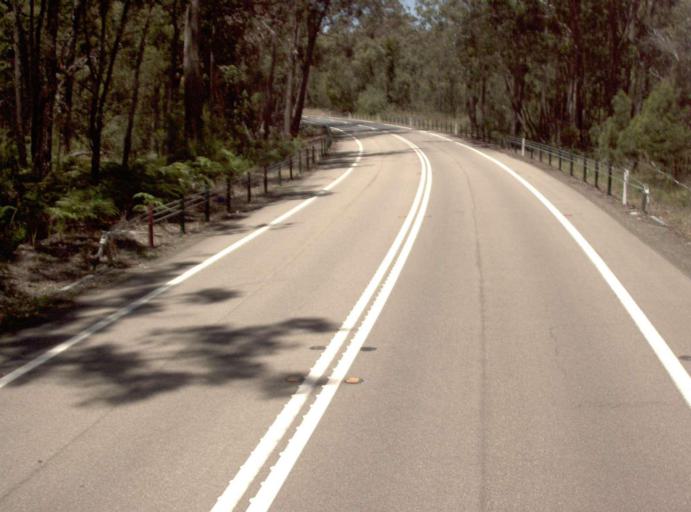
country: AU
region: Victoria
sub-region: East Gippsland
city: Lakes Entrance
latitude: -37.8199
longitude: 148.0284
